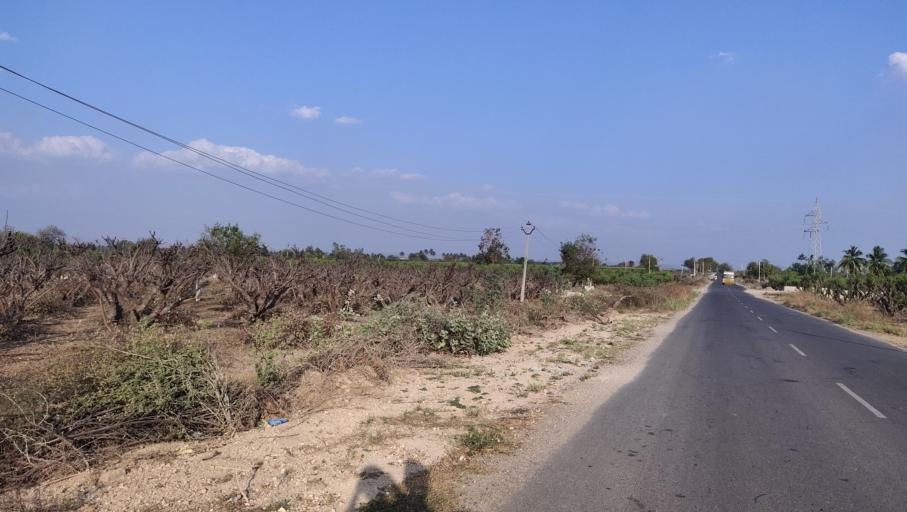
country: IN
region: Andhra Pradesh
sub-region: Anantapur
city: Tadpatri
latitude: 14.9510
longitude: 77.8862
